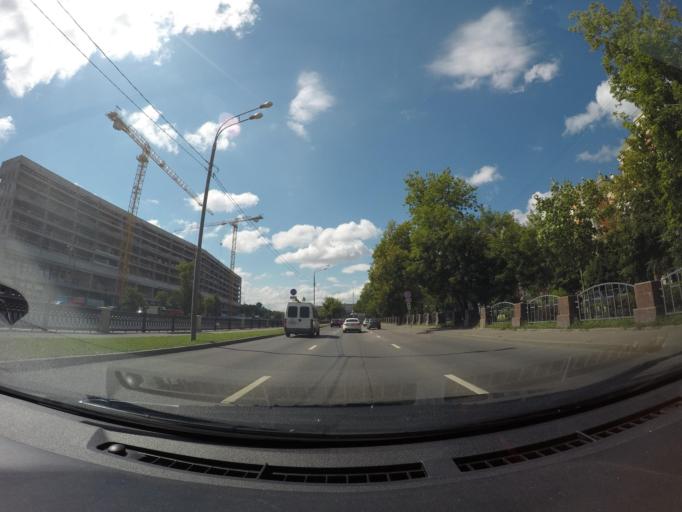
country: RU
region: Moscow
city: Lefortovo
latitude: 55.7736
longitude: 37.6964
